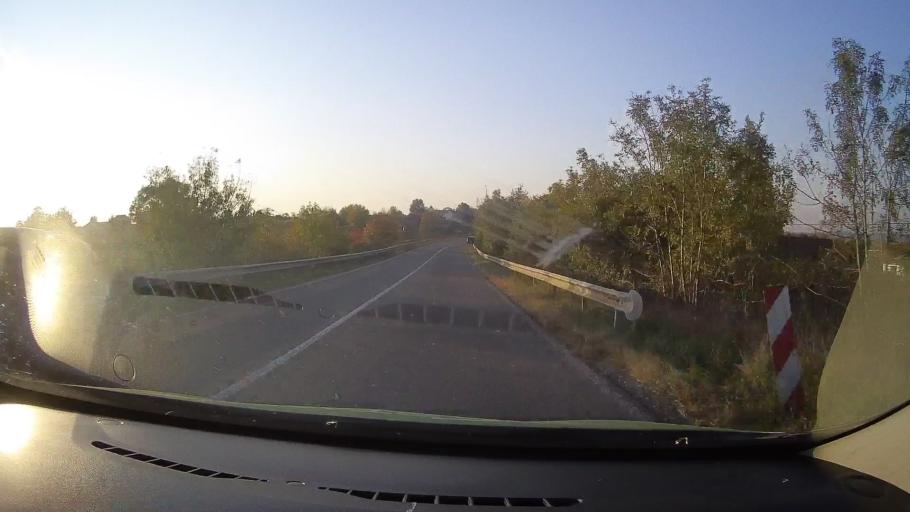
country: RO
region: Arad
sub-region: Comuna Barsa
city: Barsa
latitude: 46.3951
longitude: 22.0372
